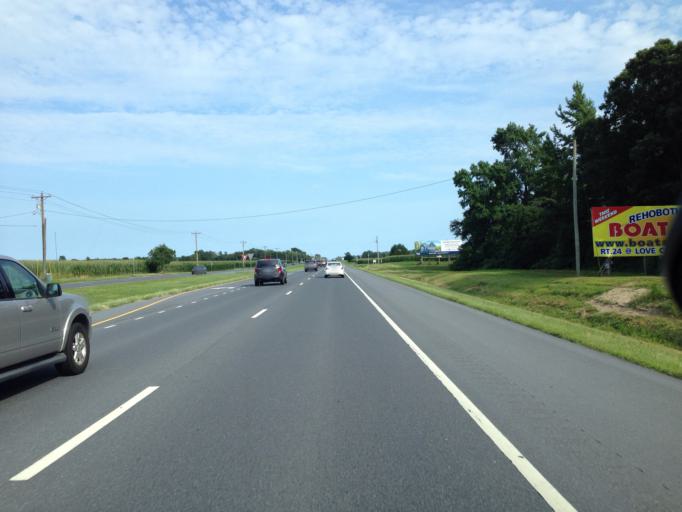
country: US
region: Delaware
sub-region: Sussex County
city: Milton
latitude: 38.7827
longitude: -75.2381
